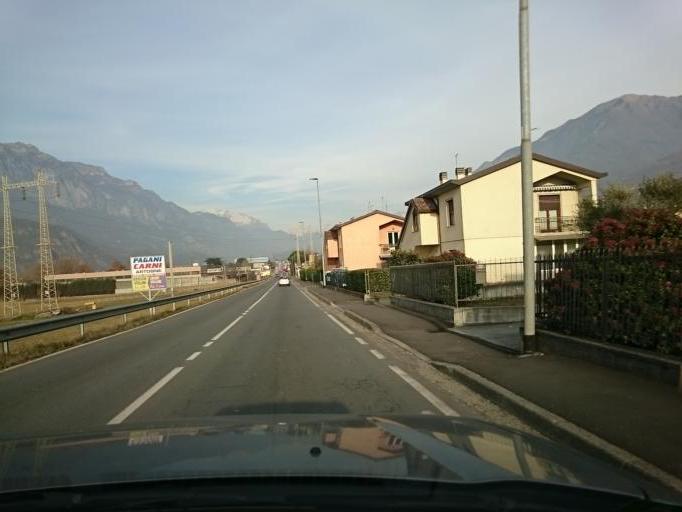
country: IT
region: Lombardy
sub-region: Provincia di Brescia
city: Artogne
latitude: 45.8545
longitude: 10.1546
